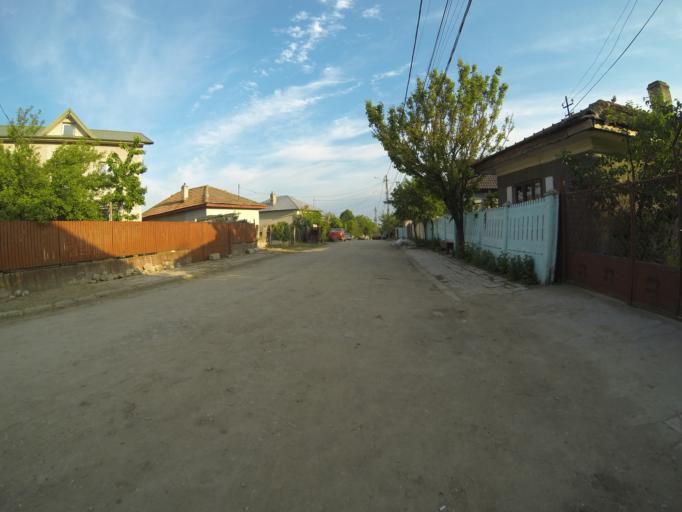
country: RO
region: Dolj
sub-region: Comuna Segarcea
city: Segarcea
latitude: 44.0982
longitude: 23.7469
